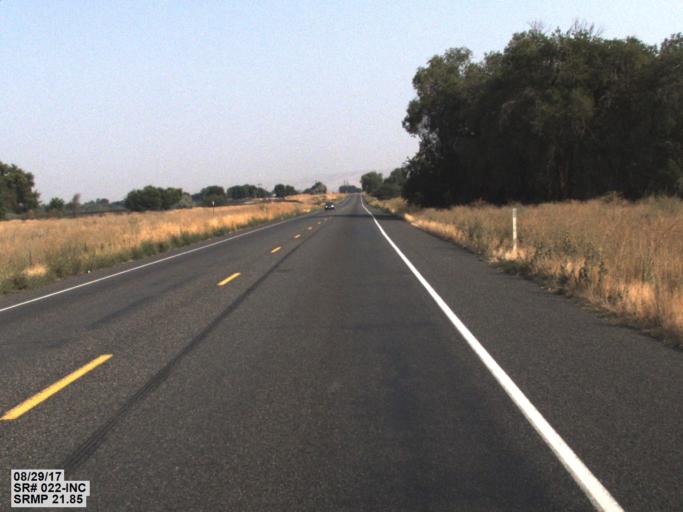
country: US
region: Washington
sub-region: Yakima County
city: Mabton
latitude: 46.2177
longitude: -120.0245
